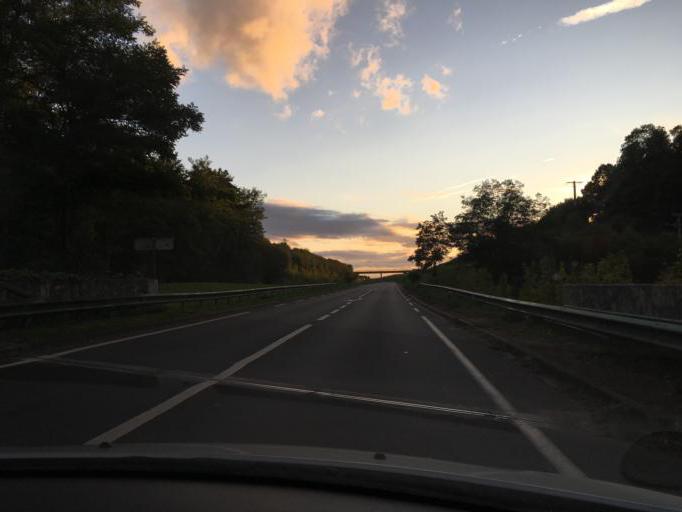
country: FR
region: Centre
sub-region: Departement d'Eure-et-Loir
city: Chateaudun
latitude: 48.0879
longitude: 1.3302
